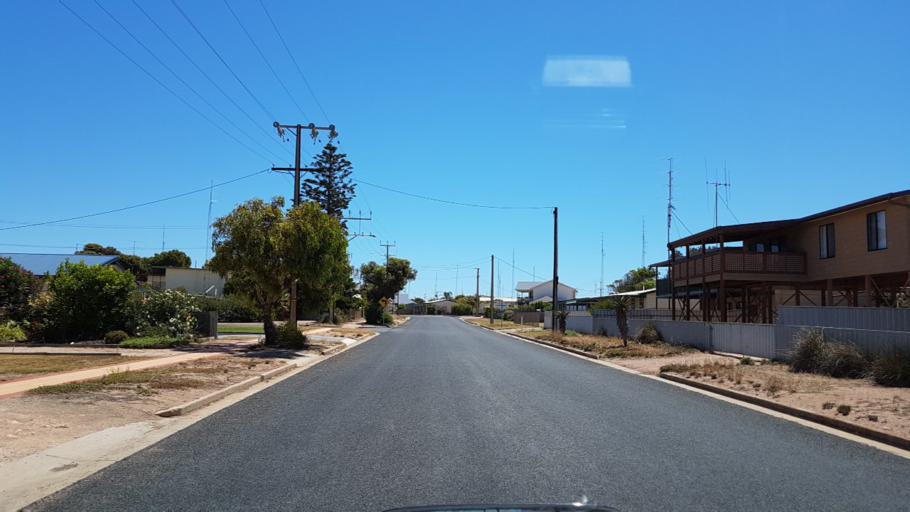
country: AU
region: South Australia
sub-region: Copper Coast
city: Wallaroo
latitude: -33.8980
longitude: 137.6299
